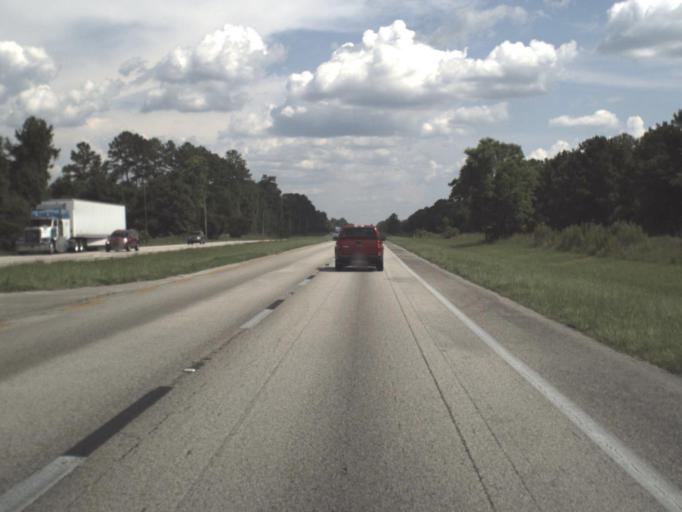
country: US
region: Florida
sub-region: Alachua County
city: Hawthorne
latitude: 29.6477
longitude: -82.1095
